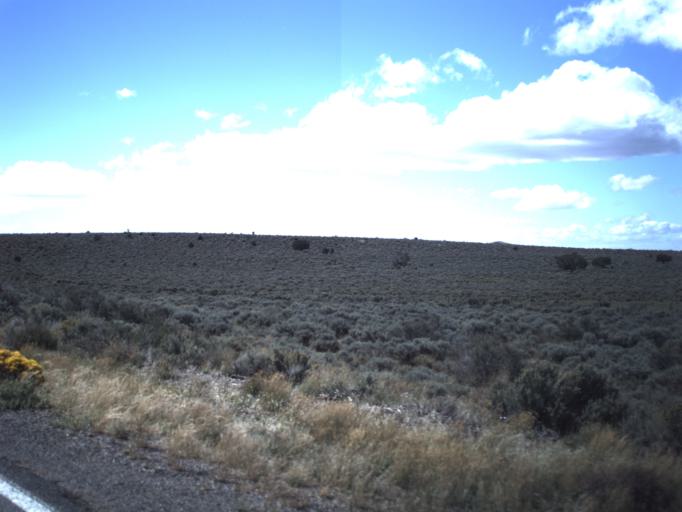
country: US
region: Utah
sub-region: Iron County
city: Parowan
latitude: 38.0730
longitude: -112.9606
